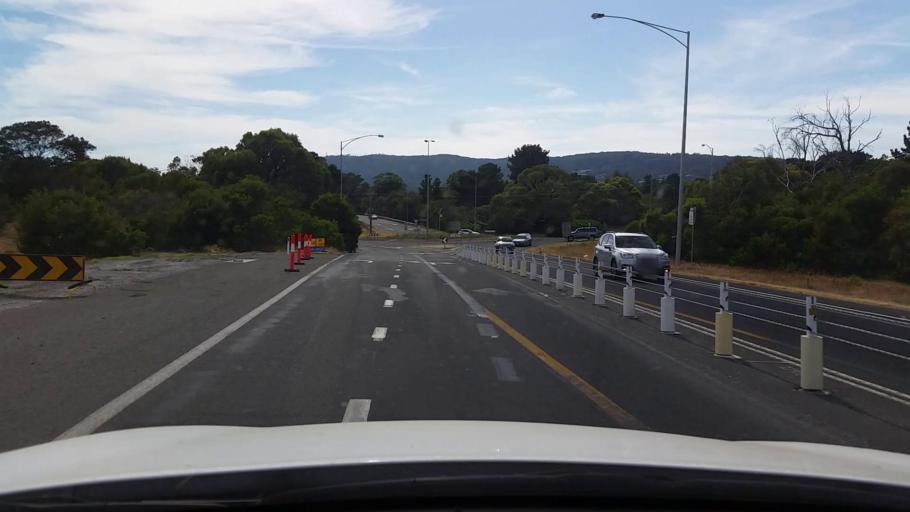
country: AU
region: Victoria
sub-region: Mornington Peninsula
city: Rosebud
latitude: -38.3706
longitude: 144.9074
